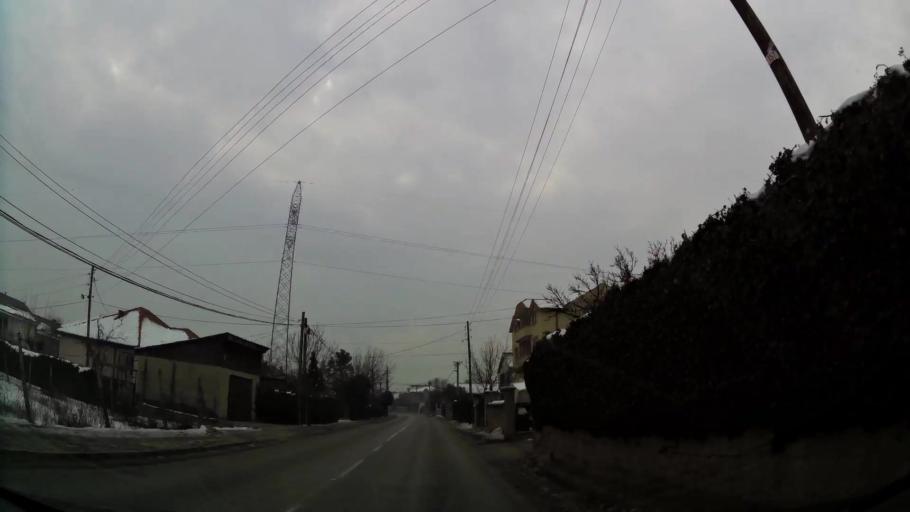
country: MK
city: Kondovo
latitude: 42.0408
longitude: 21.3475
